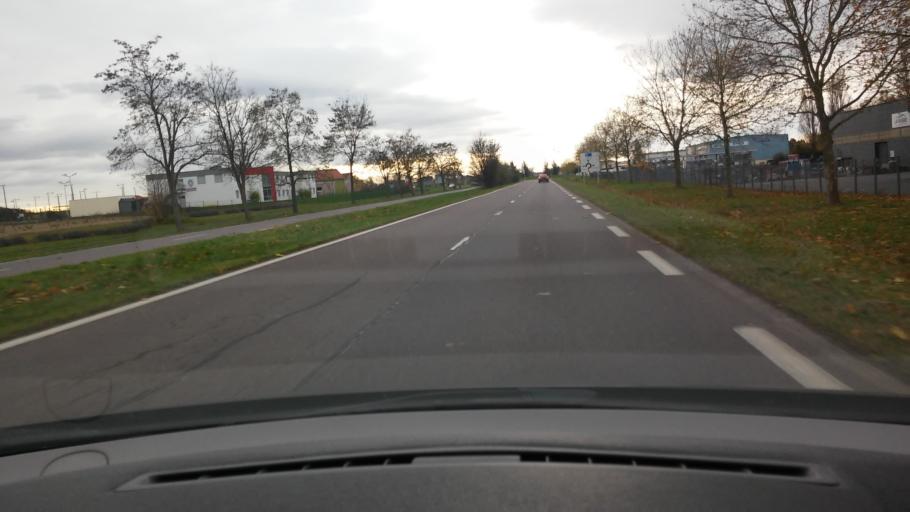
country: FR
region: Lorraine
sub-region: Departement de la Moselle
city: Ennery
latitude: 49.2227
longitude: 6.2103
